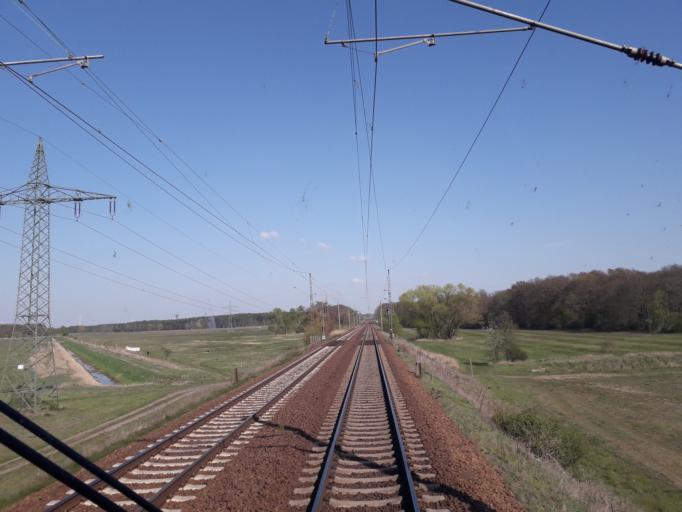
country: DE
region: Brandenburg
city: Stahnsdorf
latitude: 52.3206
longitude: 13.1707
